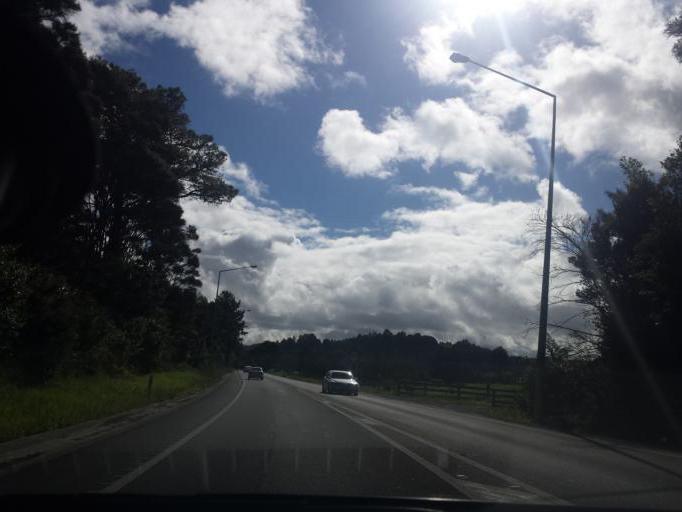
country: NZ
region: Auckland
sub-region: Auckland
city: Warkworth
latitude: -36.5202
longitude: 174.6745
